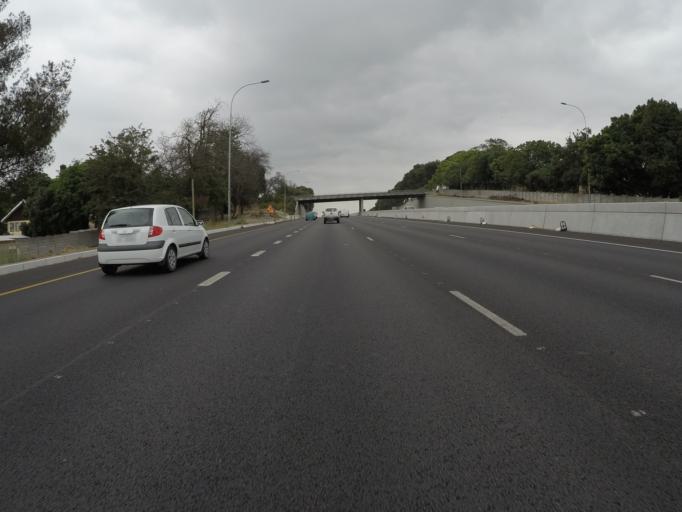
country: ZA
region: Western Cape
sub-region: City of Cape Town
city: Kraaifontein
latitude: -33.8888
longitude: 18.6197
